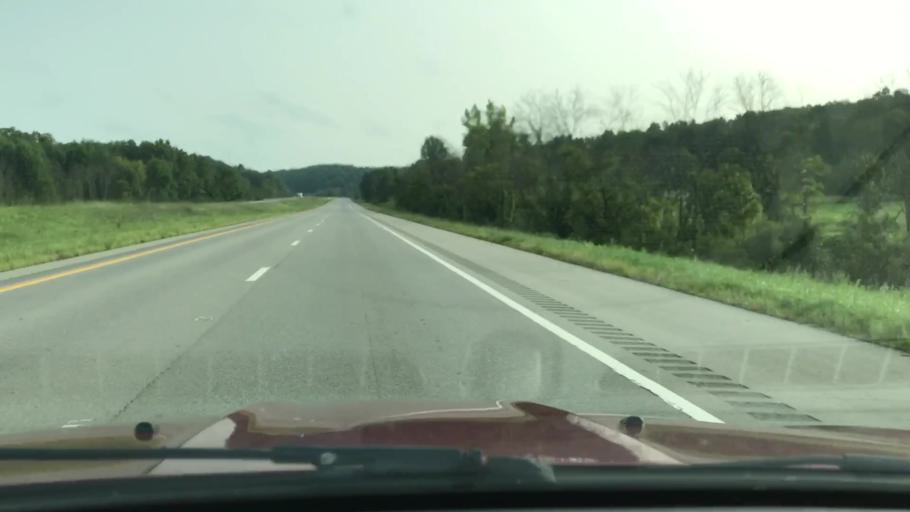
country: US
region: Ohio
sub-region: Guernsey County
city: Byesville
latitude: 39.8720
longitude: -81.5366
